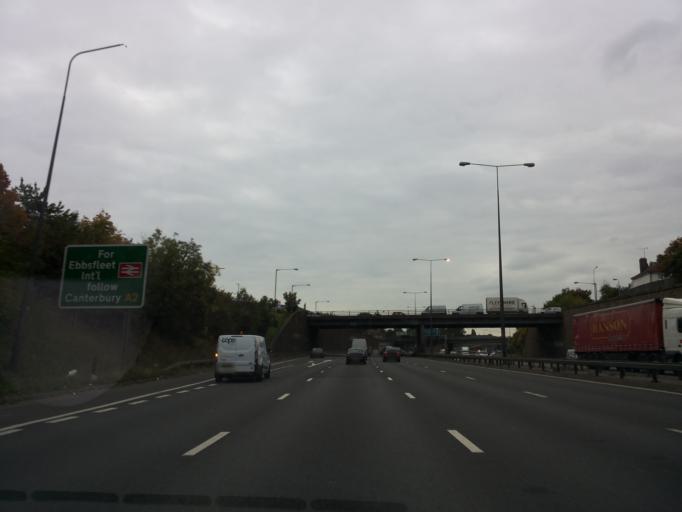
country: GB
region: England
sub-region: Kent
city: Dartford
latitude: 51.4435
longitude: 0.2374
